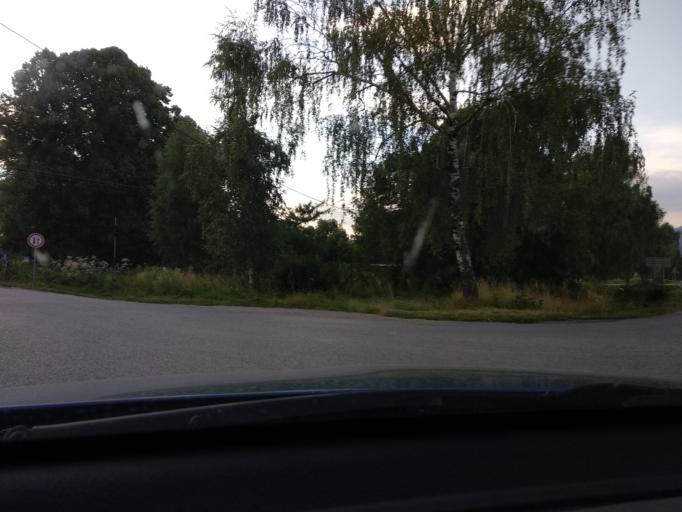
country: SK
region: Zilinsky
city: Ruzomberok
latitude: 49.0620
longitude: 19.3360
